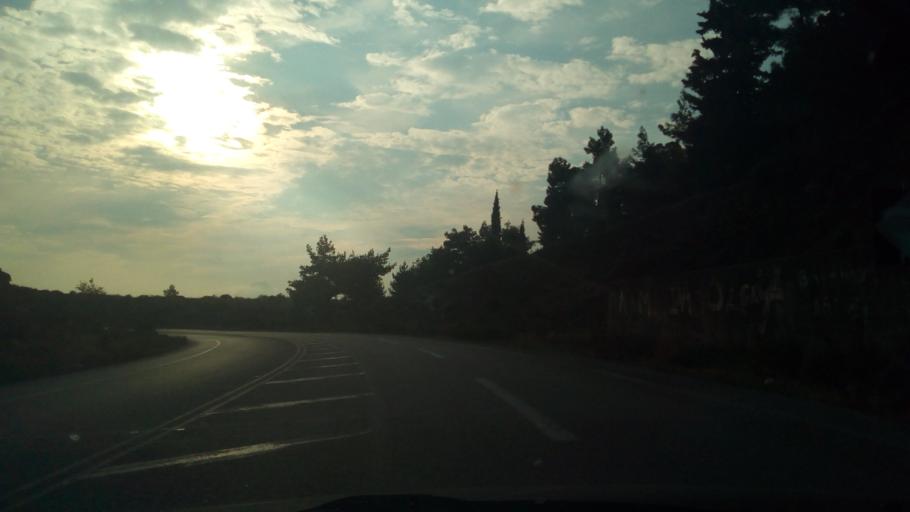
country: GR
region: West Greece
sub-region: Nomos Aitolias kai Akarnanias
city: Nafpaktos
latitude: 38.3993
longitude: 21.8226
